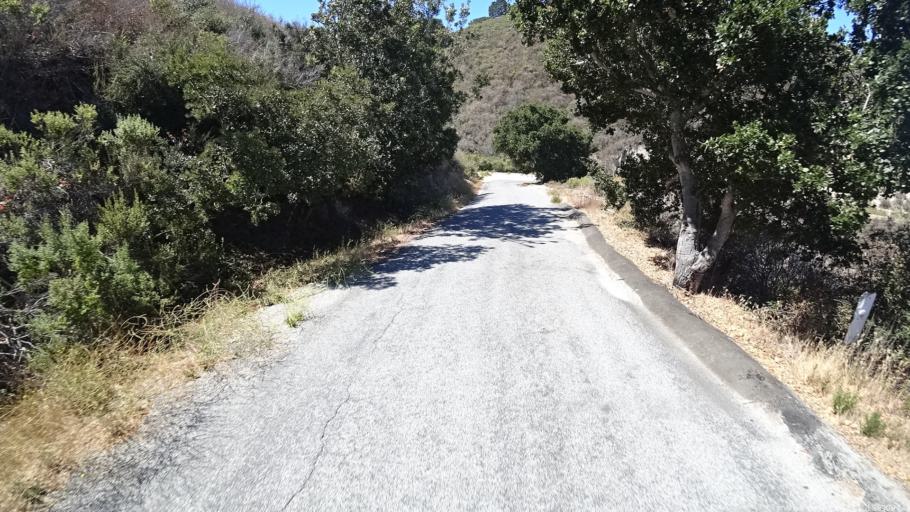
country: US
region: California
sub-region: Monterey County
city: Carmel Valley Village
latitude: 36.5527
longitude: -121.7482
